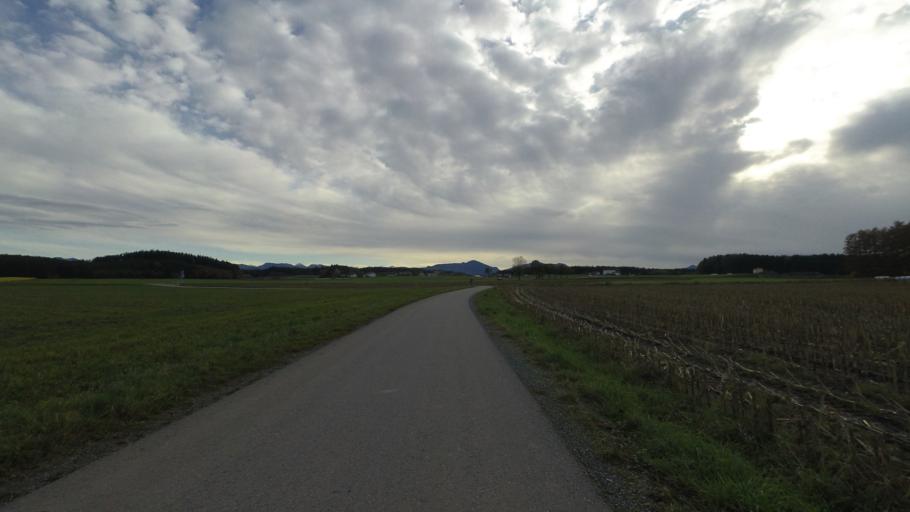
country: DE
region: Bavaria
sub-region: Upper Bavaria
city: Nussdorf
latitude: 47.9315
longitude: 12.5918
